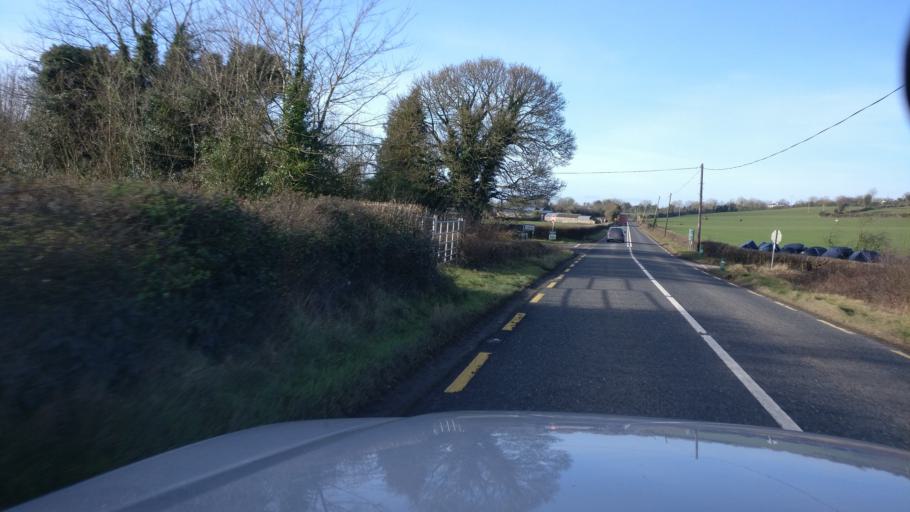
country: IE
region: Leinster
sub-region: Uibh Fhaili
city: Tullamore
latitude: 53.1940
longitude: -7.4136
